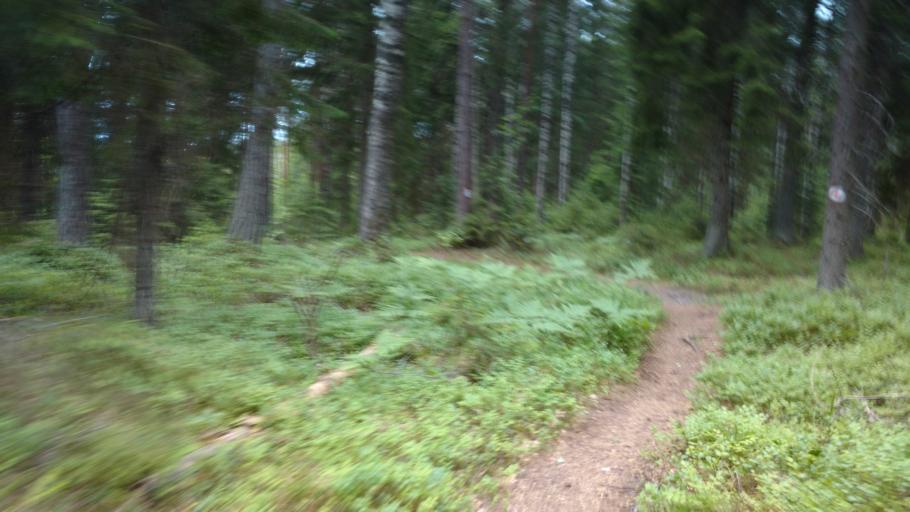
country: FI
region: Uusimaa
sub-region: Raaseporin
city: Pohja
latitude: 60.1164
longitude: 23.5519
